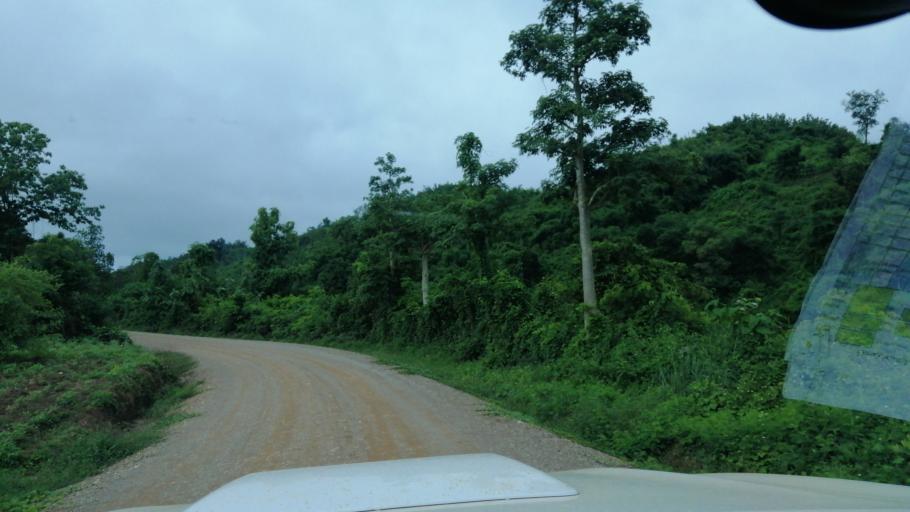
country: LA
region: Xiagnabouli
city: Muang Kenthao
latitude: 17.9697
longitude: 101.4119
